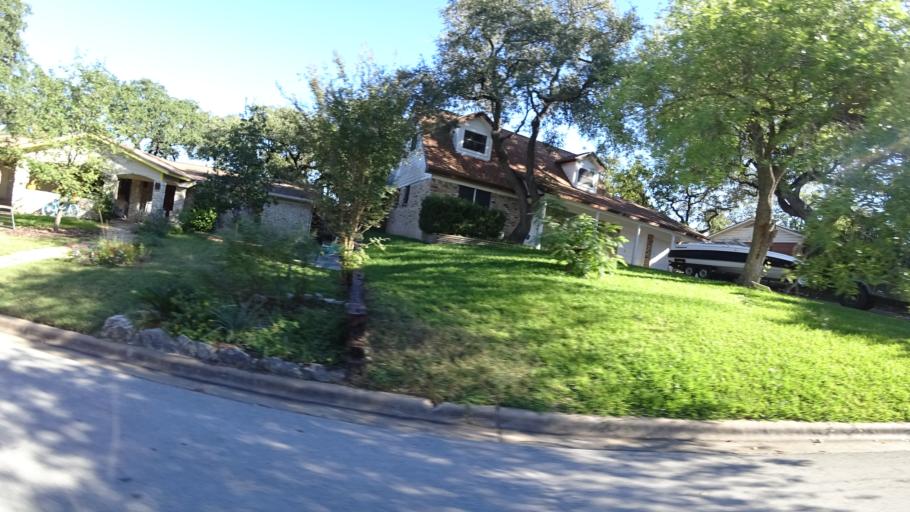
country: US
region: Texas
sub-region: Travis County
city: Rollingwood
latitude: 30.2362
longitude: -97.8067
